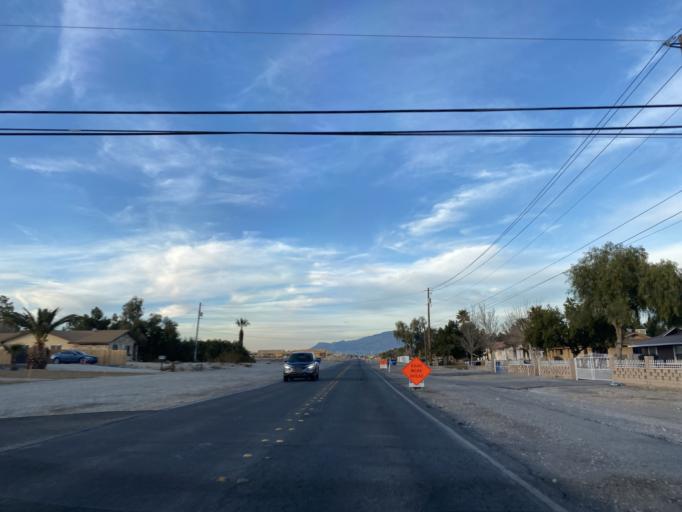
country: US
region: Nevada
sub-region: Clark County
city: Summerlin South
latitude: 36.2645
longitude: -115.2974
